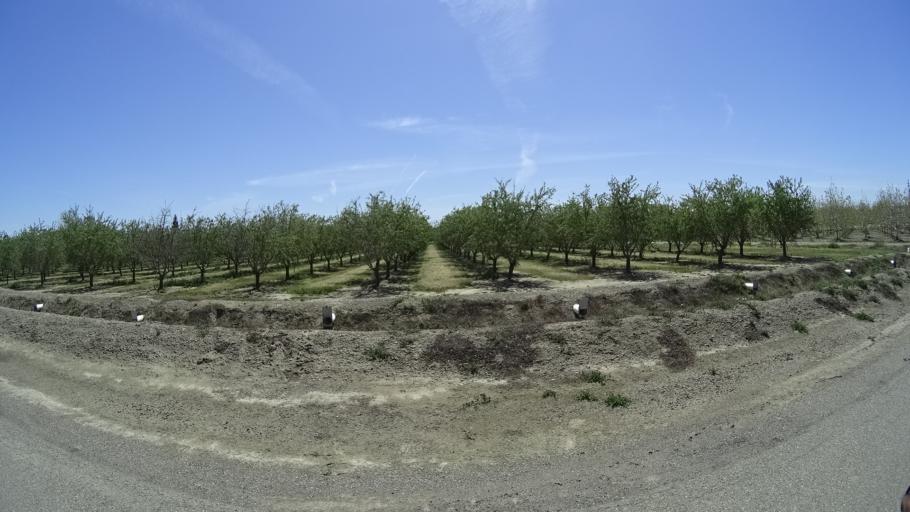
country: US
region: California
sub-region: Glenn County
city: Orland
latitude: 39.7321
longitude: -122.1062
